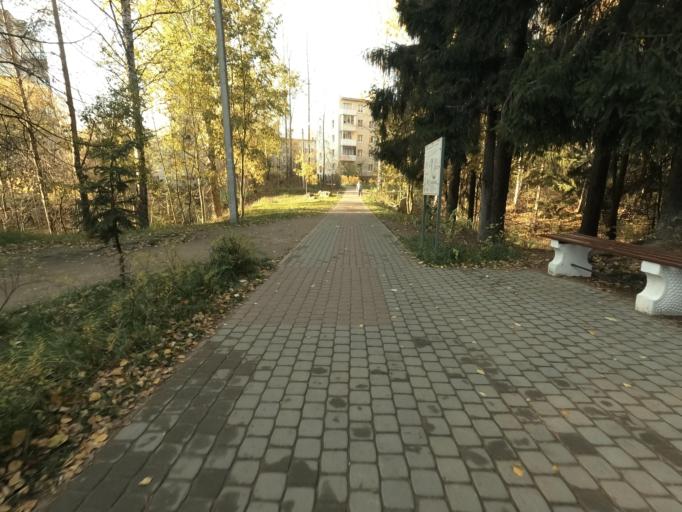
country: RU
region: Leningrad
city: Sertolovo
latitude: 60.1495
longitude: 30.2079
